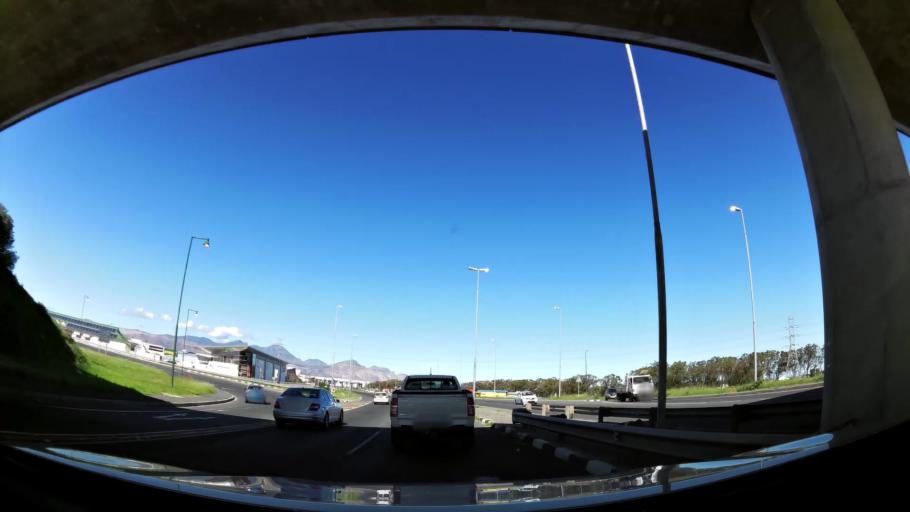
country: ZA
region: Western Cape
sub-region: Cape Winelands District Municipality
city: Stellenbosch
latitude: -34.0816
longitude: 18.8191
